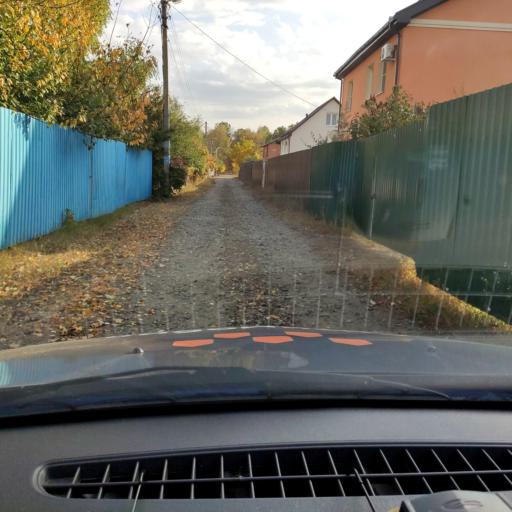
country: RU
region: Voronezj
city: Podgornoye
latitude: 51.7964
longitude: 39.2150
